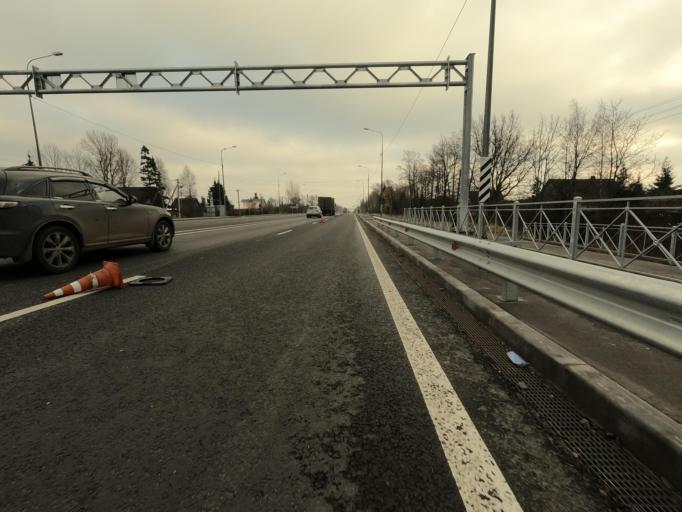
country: RU
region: Leningrad
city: Mga
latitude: 59.7226
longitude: 31.0975
